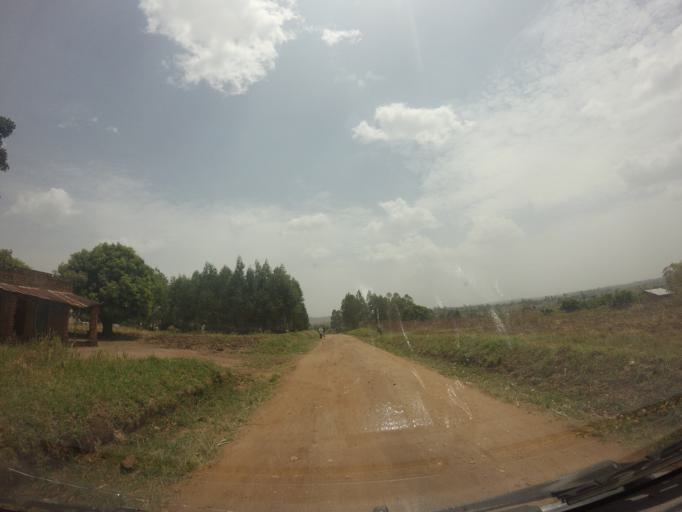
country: UG
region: Northern Region
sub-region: Arua District
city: Arua
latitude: 2.9378
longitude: 30.9156
